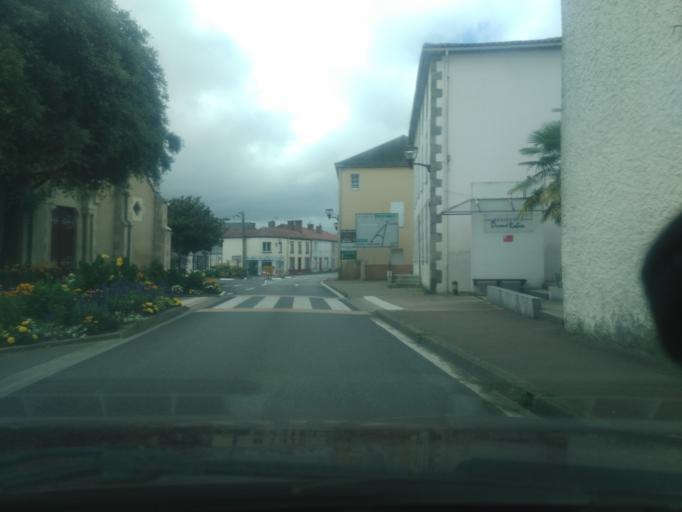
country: FR
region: Pays de la Loire
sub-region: Departement de la Vendee
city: La Ferriere
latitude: 46.7133
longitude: -1.3141
